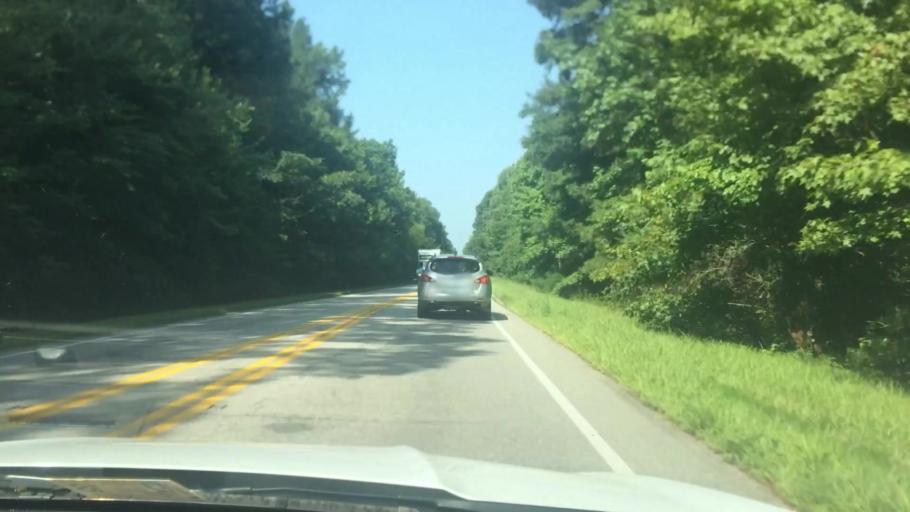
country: US
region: Virginia
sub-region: City of Poquoson
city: Poquoson
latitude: 37.1230
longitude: -76.4216
